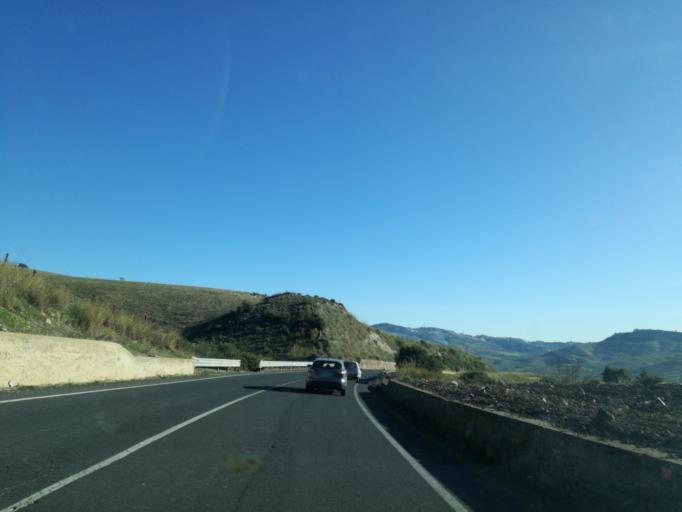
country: IT
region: Sicily
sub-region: Catania
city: San Michele di Ganzaria
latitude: 37.2301
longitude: 14.4411
